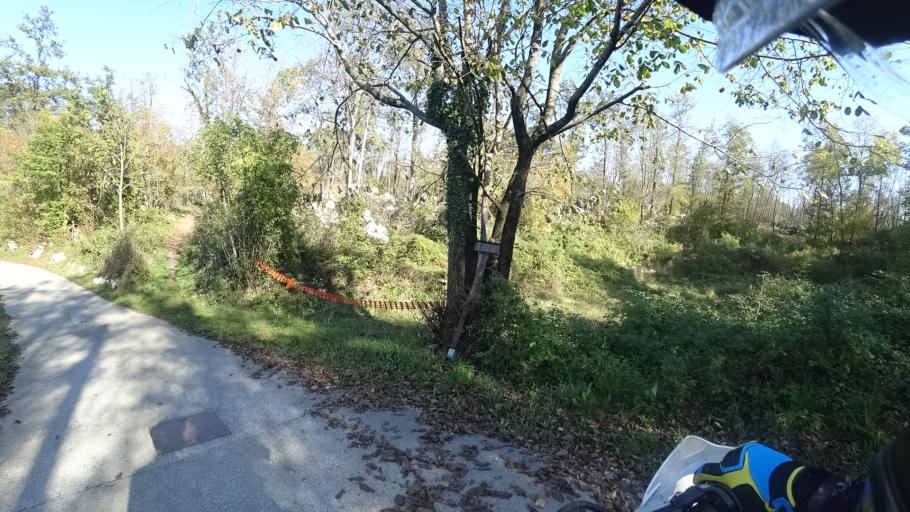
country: HR
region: Primorsko-Goranska
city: Kastav
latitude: 45.3935
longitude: 14.3267
